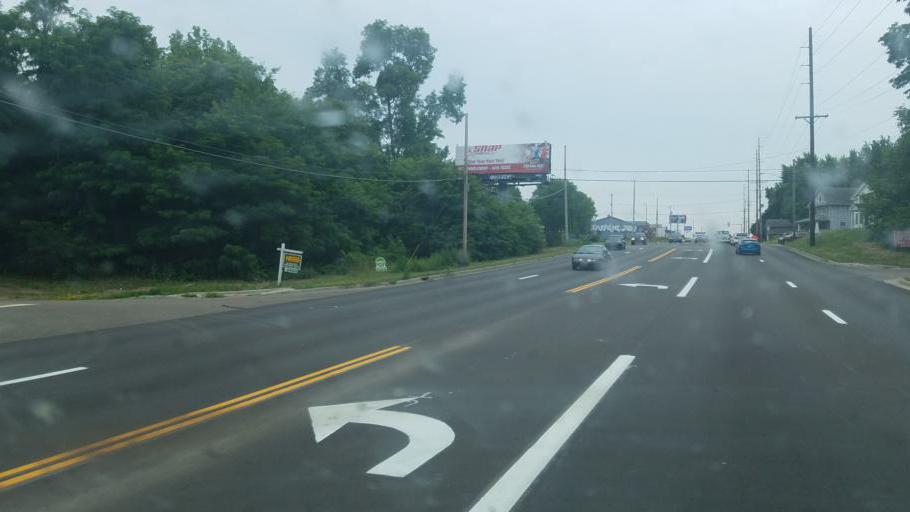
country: US
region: Ohio
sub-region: Summit County
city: Portage Lakes
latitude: 41.0192
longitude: -81.5506
